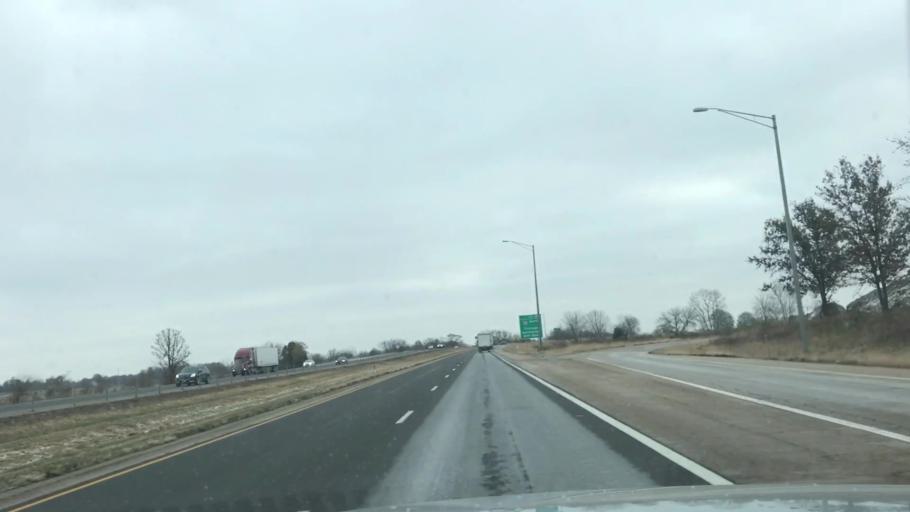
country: US
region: Illinois
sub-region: Madison County
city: Troy
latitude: 38.7520
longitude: -89.9131
